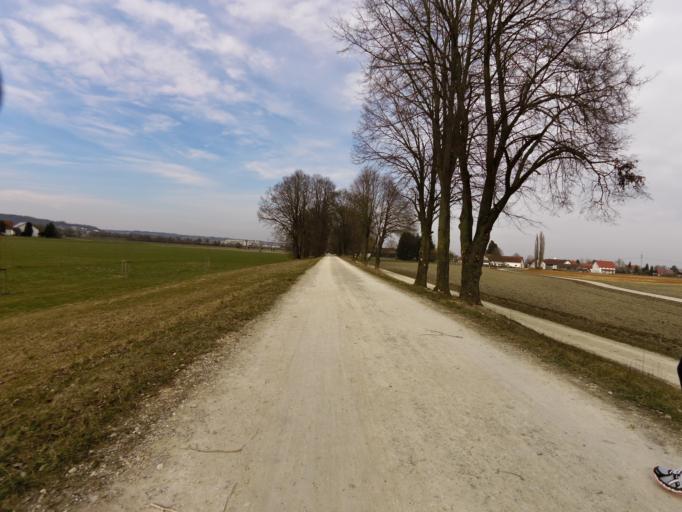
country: DE
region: Bavaria
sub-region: Lower Bavaria
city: Tiefenbach
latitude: 48.5328
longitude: 12.1112
